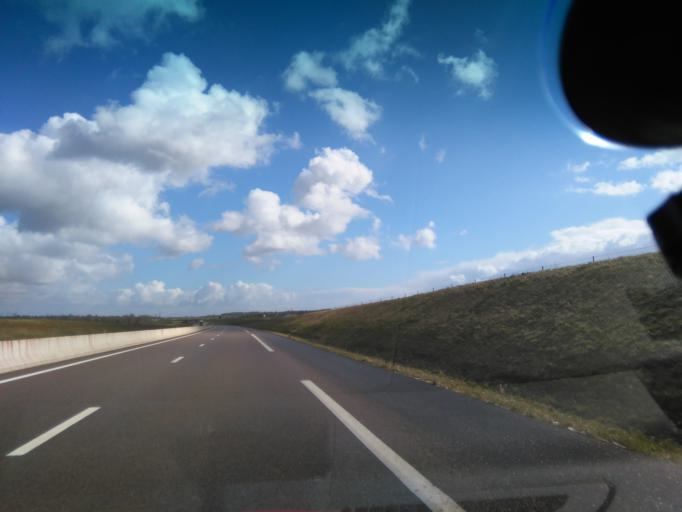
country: FR
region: Lower Normandy
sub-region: Departement de l'Orne
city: Argentan
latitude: 48.6944
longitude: -0.0228
